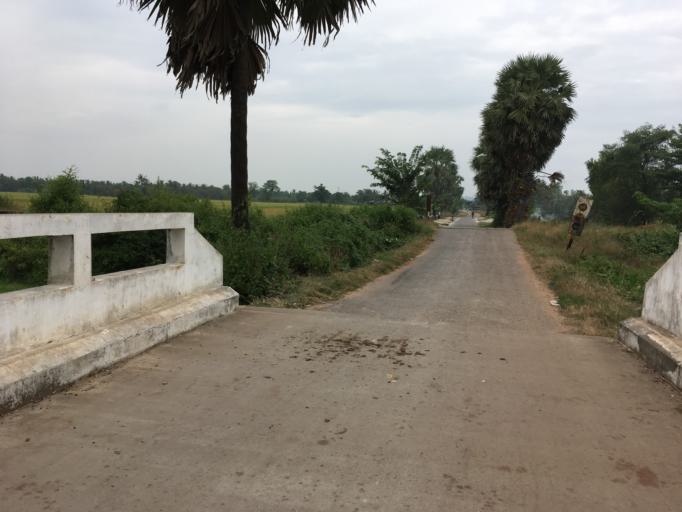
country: MM
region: Mon
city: Mawlamyine
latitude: 16.4330
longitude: 97.6295
